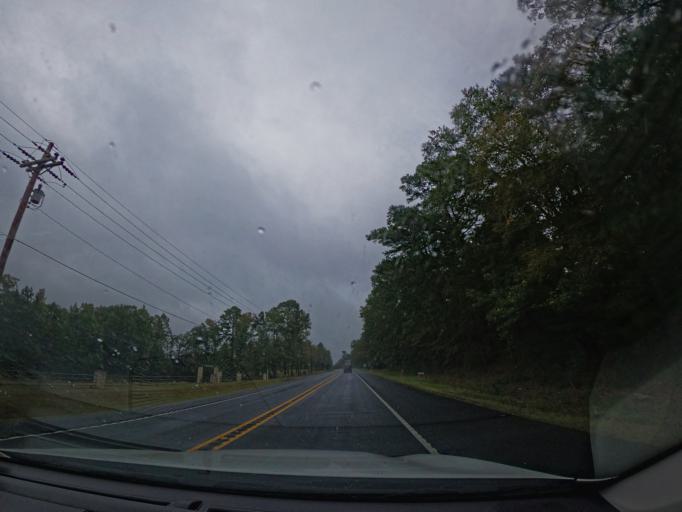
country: US
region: Louisiana
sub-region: Caddo Parish
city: Greenwood
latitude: 32.3999
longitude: -94.0008
